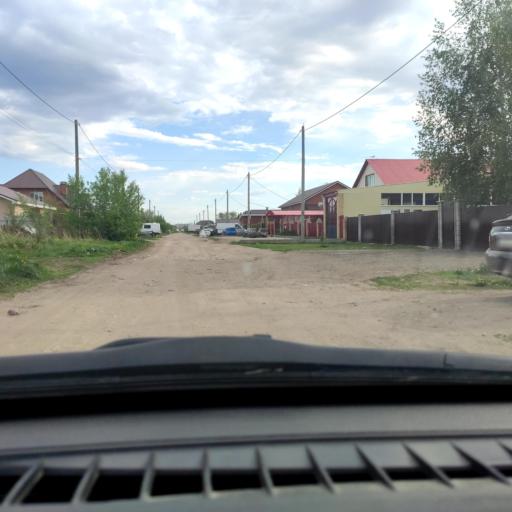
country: RU
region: Samara
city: Tol'yatti
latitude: 53.5714
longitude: 49.4111
